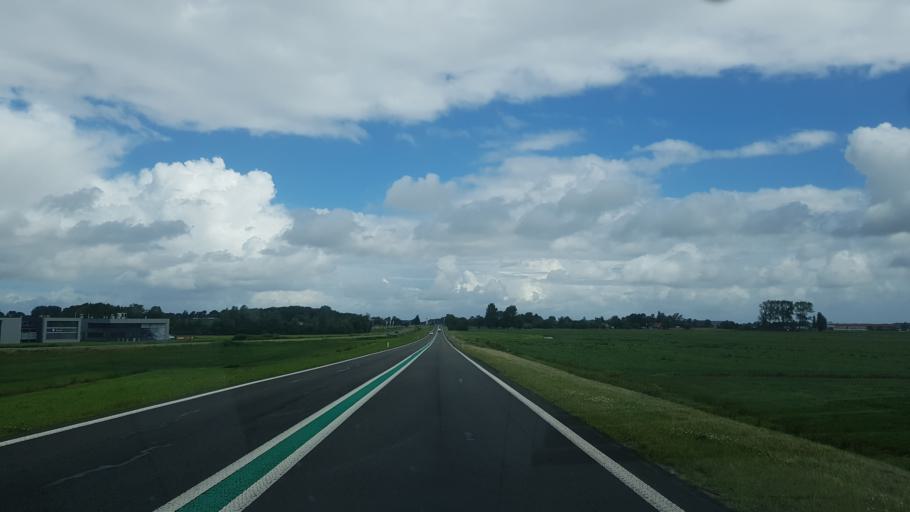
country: NL
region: Friesland
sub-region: Gemeente Dantumadiel
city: Walterswald
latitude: 53.3186
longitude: 6.0218
